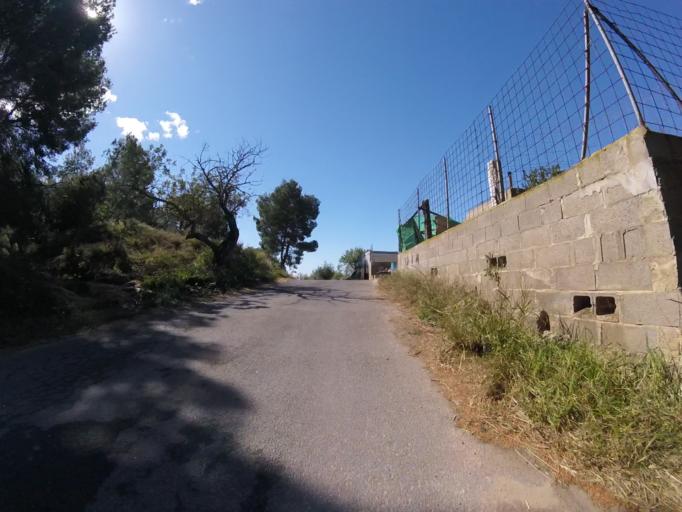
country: ES
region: Valencia
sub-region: Provincia de Castello
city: Benicassim
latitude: 40.0696
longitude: 0.0749
